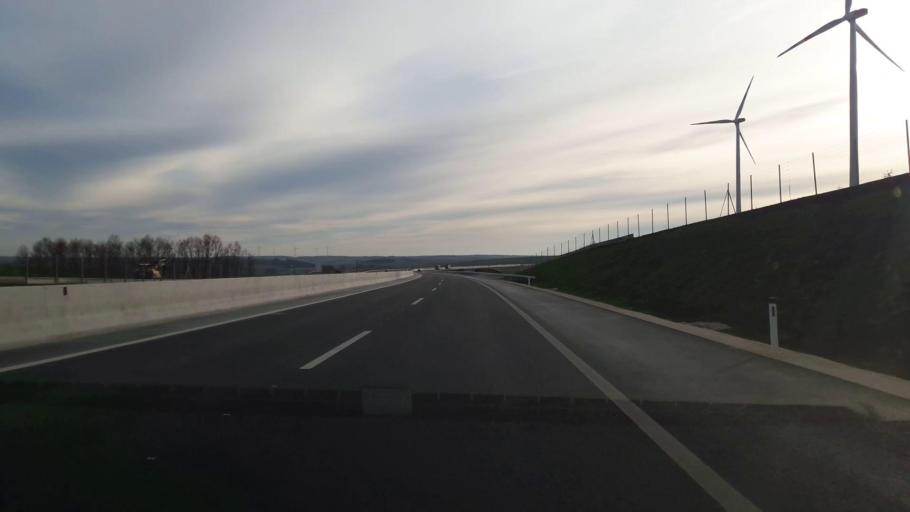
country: AT
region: Lower Austria
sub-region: Politischer Bezirk Mistelbach
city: Grosskrut
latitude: 48.6234
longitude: 16.6758
